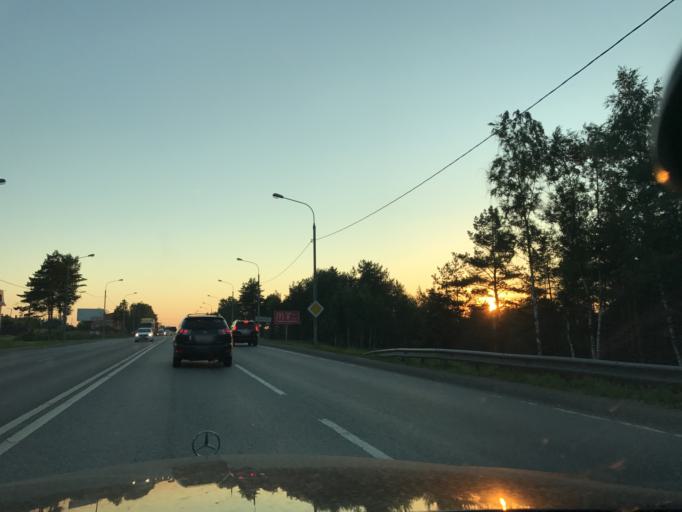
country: RU
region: Vladimir
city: Pokrov
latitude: 55.9207
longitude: 39.2113
